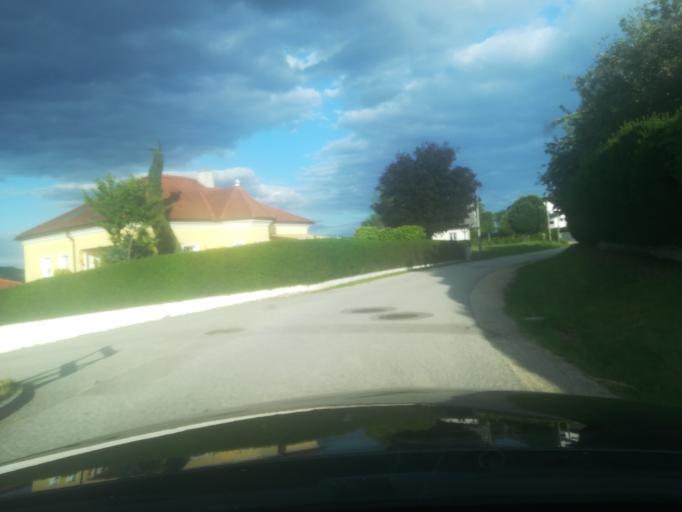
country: AT
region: Upper Austria
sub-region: Politischer Bezirk Urfahr-Umgebung
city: Engerwitzdorf
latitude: 48.3655
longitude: 14.5523
